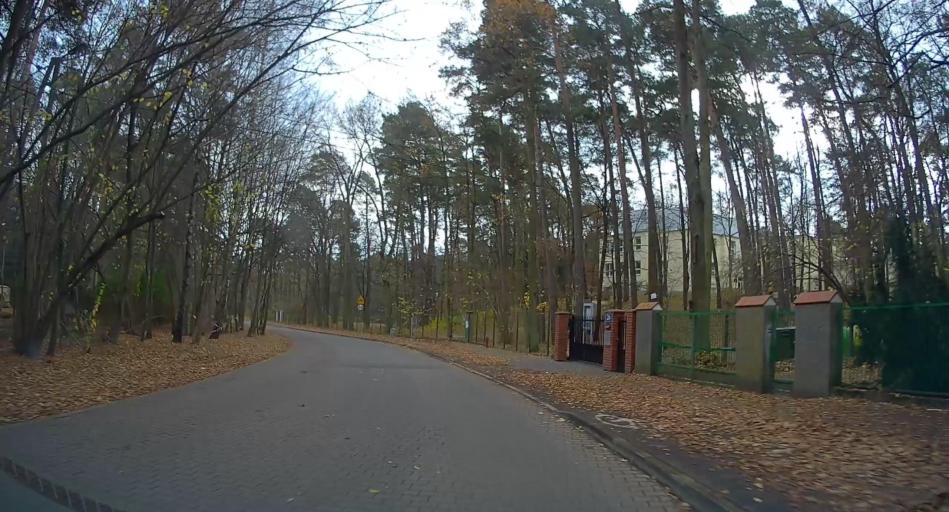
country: PL
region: Masovian Voivodeship
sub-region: Powiat piaseczynski
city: Piaseczno
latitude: 52.0547
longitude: 21.0201
